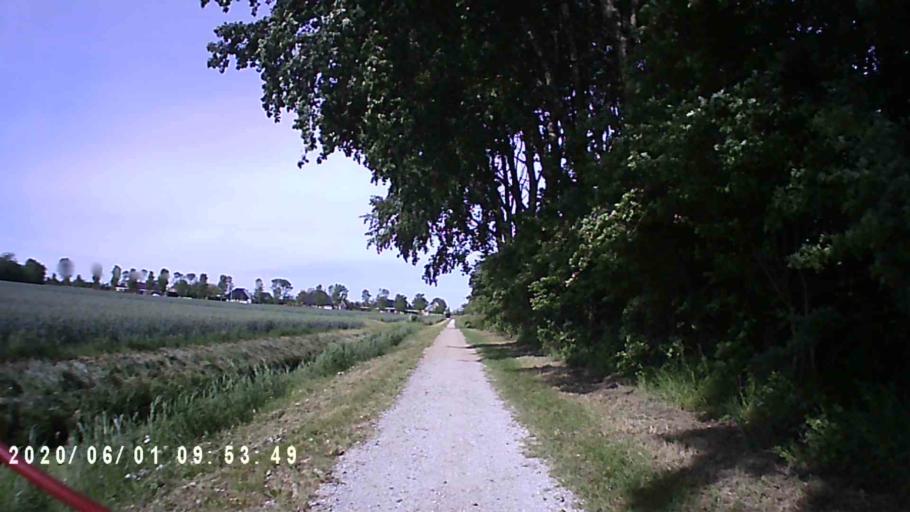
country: NL
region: Friesland
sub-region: Menameradiel
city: Berltsum
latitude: 53.2393
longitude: 5.6545
